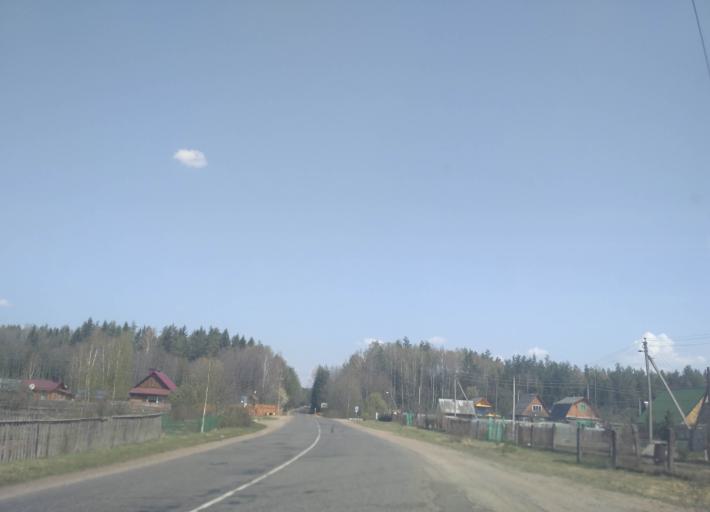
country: BY
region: Minsk
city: Loshnitsa
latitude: 54.4211
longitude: 28.6468
